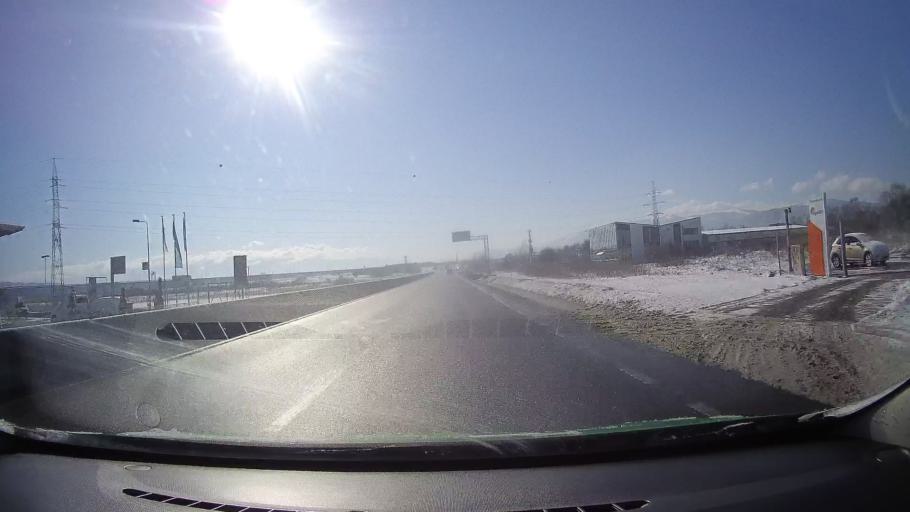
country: RO
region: Sibiu
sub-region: Comuna Selimbar
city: Selimbar
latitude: 45.7532
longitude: 24.1999
